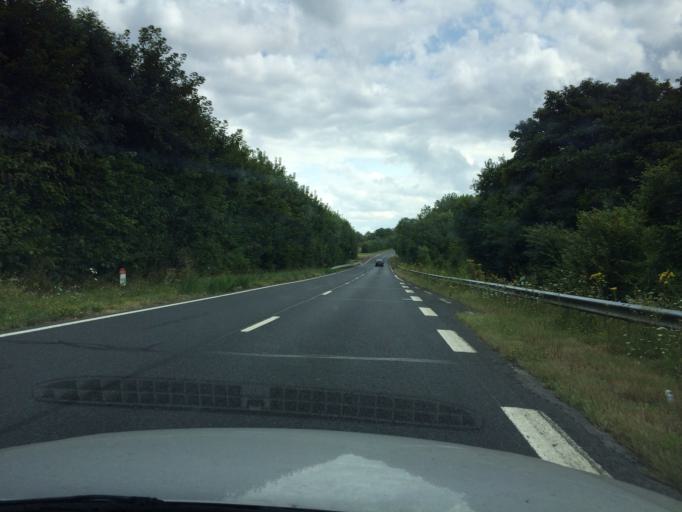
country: FR
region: Lower Normandy
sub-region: Departement du Calvados
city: Le Molay-Littry
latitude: 49.3203
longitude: -0.8577
